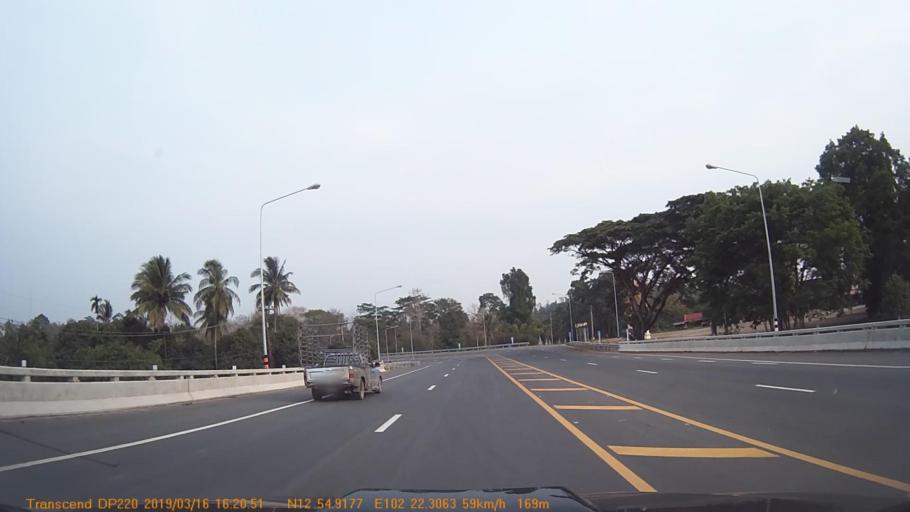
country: TH
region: Chanthaburi
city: Pong Nam Ron
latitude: 12.9151
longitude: 102.3720
